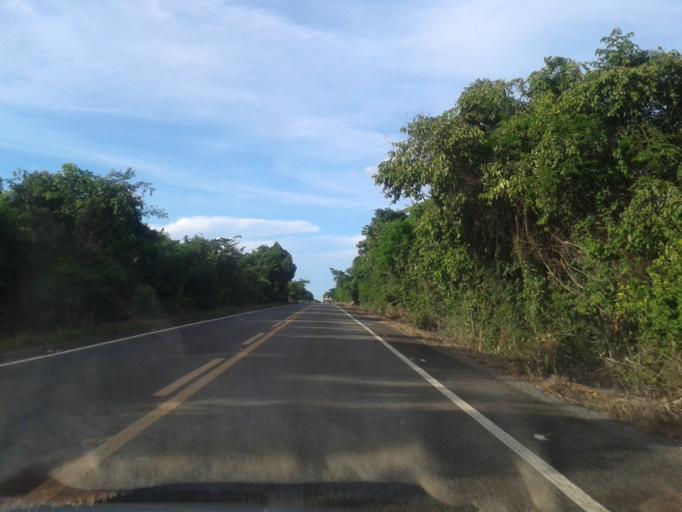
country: BR
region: Goias
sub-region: Sao Miguel Do Araguaia
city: Sao Miguel do Araguaia
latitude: -13.7066
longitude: -50.3328
